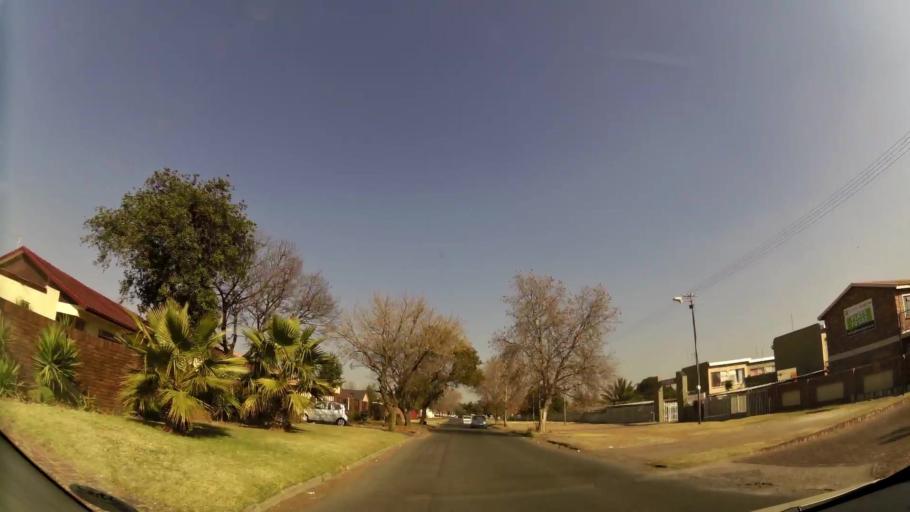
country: ZA
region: Gauteng
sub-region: West Rand District Municipality
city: Randfontein
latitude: -26.1636
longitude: 27.6988
